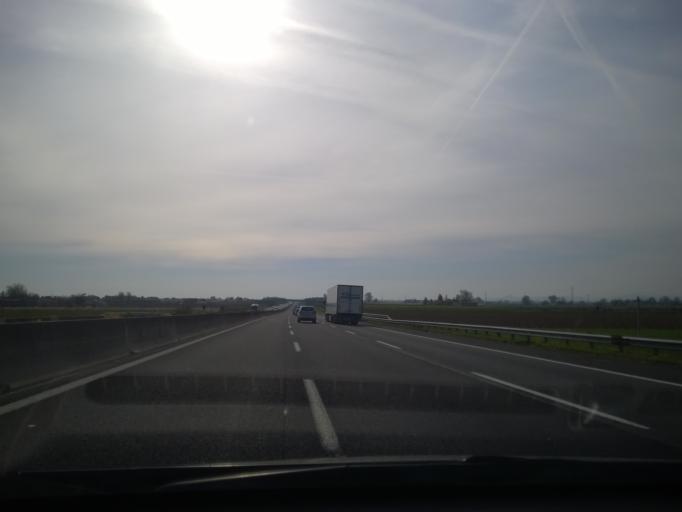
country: IT
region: Emilia-Romagna
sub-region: Provincia di Ravenna
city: Granarolo
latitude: 44.3061
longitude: 11.9473
